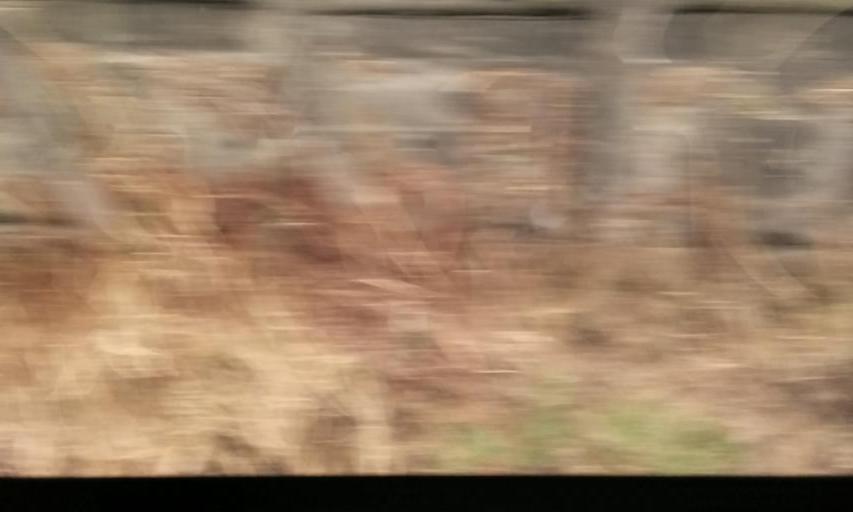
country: JP
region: Nagano
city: Tatsuno
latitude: 36.0077
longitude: 137.8563
